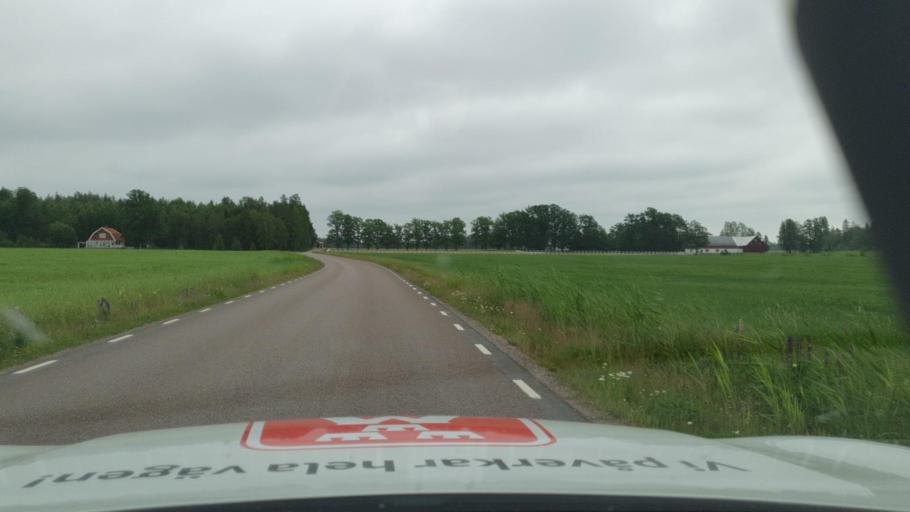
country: SE
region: Vaermland
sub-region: Kristinehamns Kommun
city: Kristinehamn
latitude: 59.4130
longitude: 13.8819
